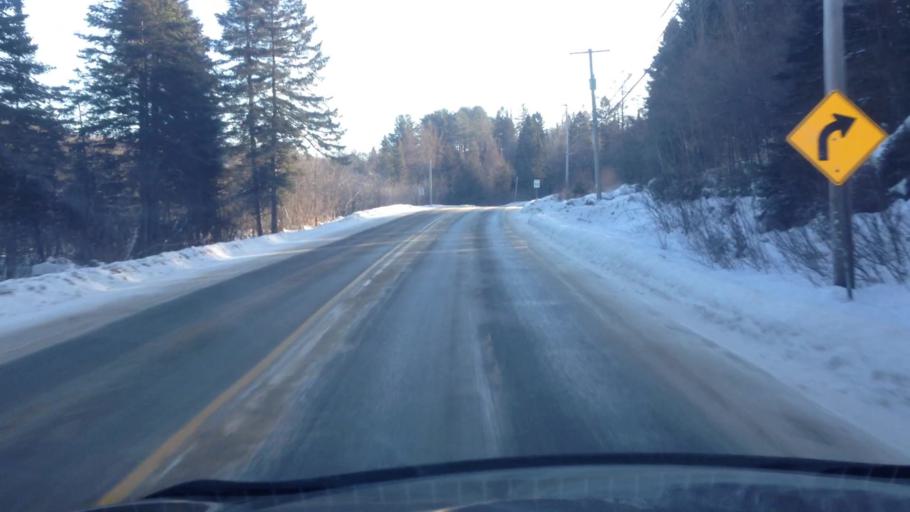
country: CA
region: Quebec
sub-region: Laurentides
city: Sainte-Agathe-des-Monts
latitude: 45.9204
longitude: -74.3824
